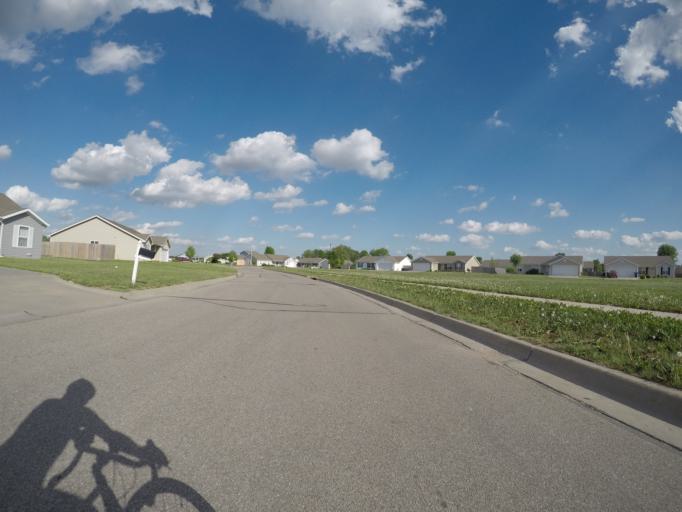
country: US
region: Kansas
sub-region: Riley County
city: Manhattan
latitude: 39.2150
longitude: -96.5601
